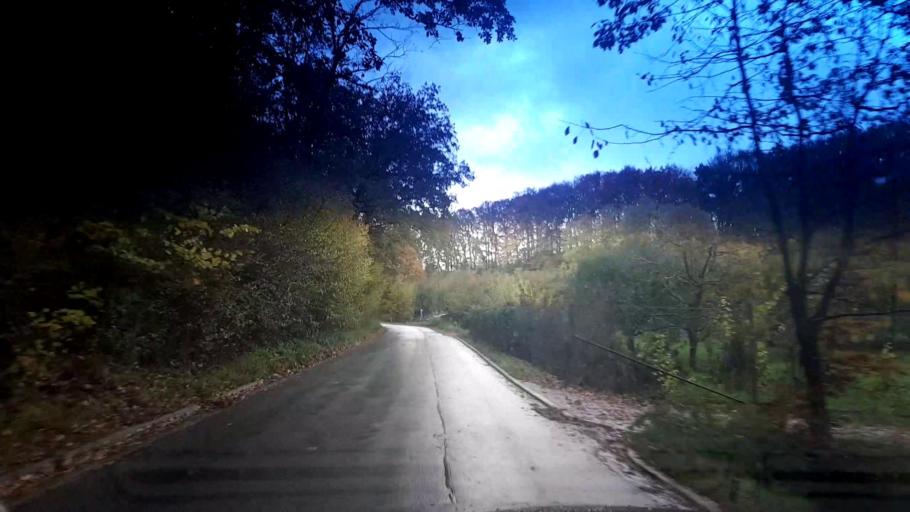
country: DE
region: Bavaria
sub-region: Upper Franconia
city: Viereth-Trunstadt
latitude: 49.9163
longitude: 10.7783
